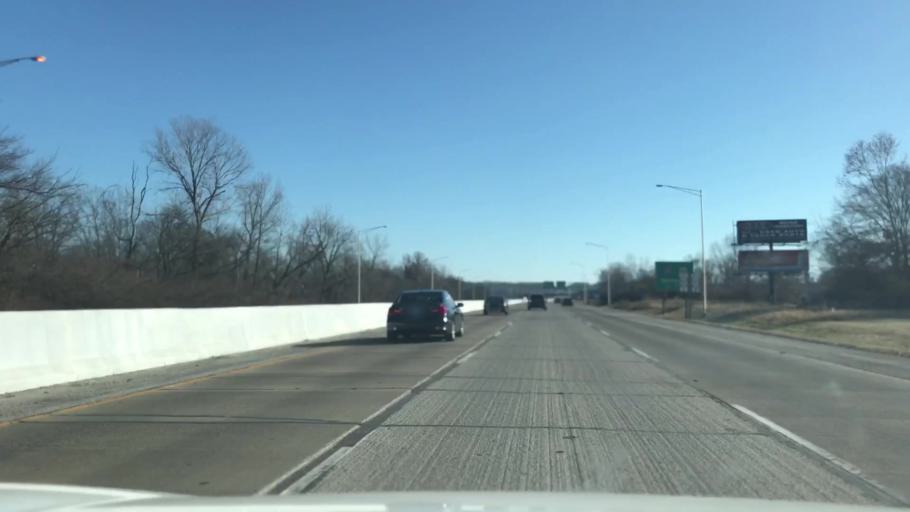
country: US
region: Illinois
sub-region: Saint Clair County
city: Alorton
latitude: 38.5894
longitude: -90.1157
